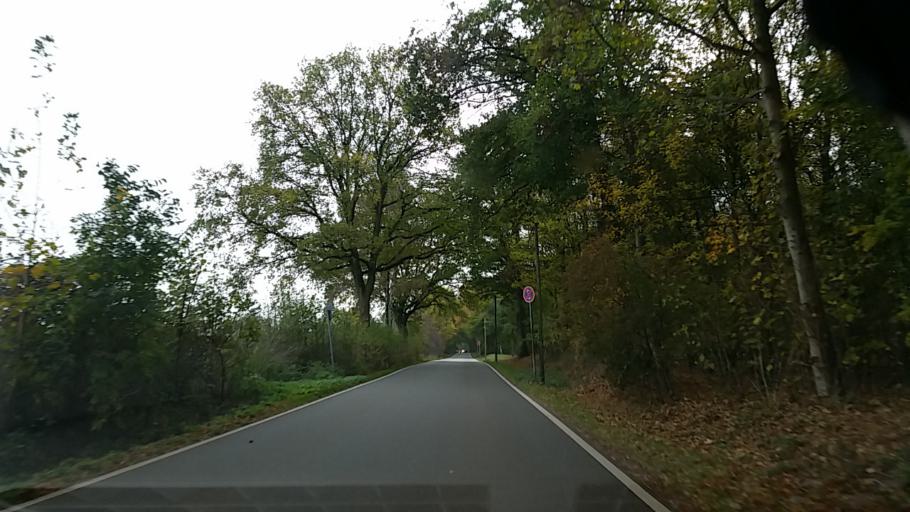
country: DE
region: Schleswig-Holstein
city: Barsbuettel
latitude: 53.5594
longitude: 10.1495
